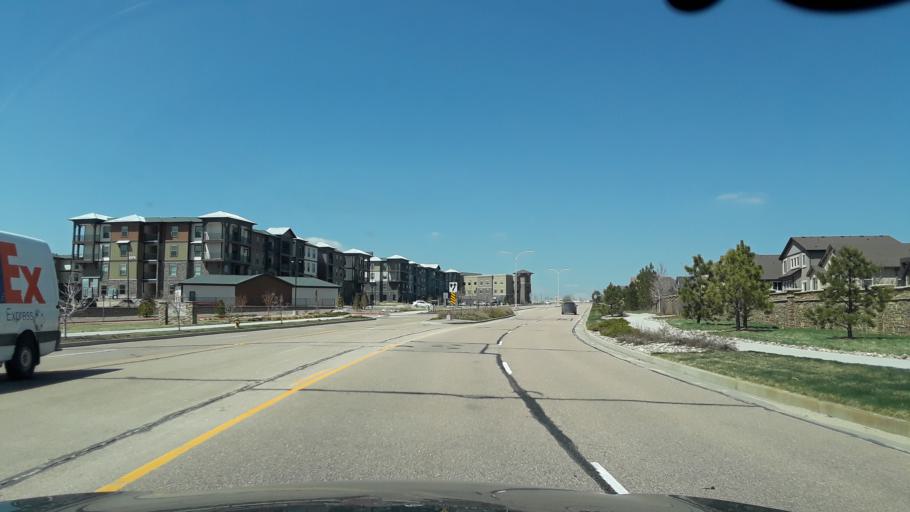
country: US
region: Colorado
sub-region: El Paso County
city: Black Forest
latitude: 38.9620
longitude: -104.7305
